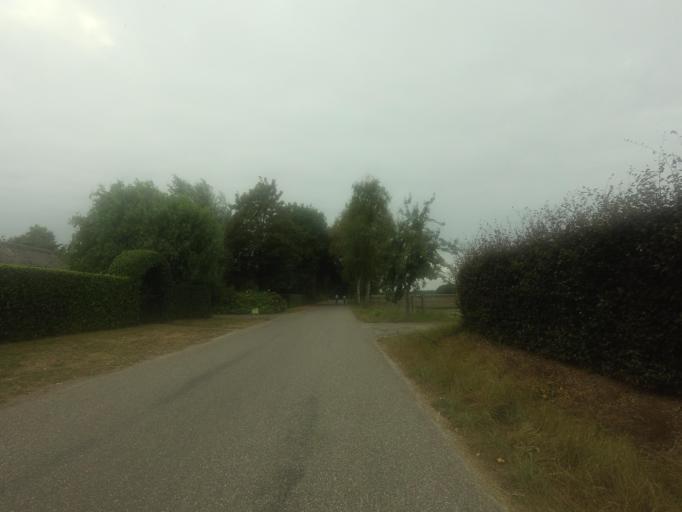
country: NL
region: North Brabant
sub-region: Gemeente Landerd
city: Zeeland
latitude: 51.7008
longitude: 5.6588
